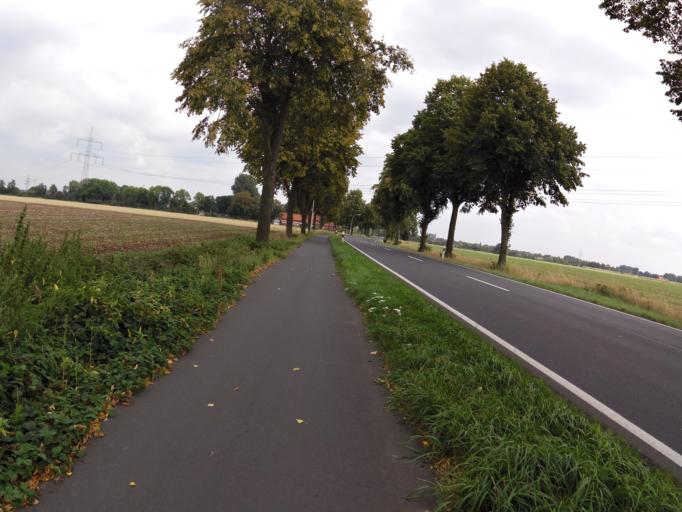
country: DE
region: Lower Saxony
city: Verden
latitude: 52.9215
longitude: 9.1965
